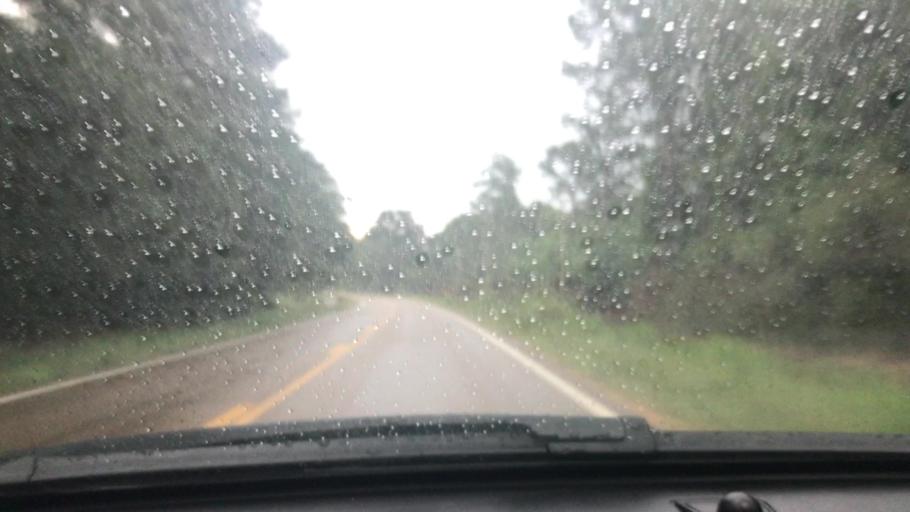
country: US
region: Mississippi
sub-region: Pike County
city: Summit
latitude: 31.2931
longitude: -90.4985
